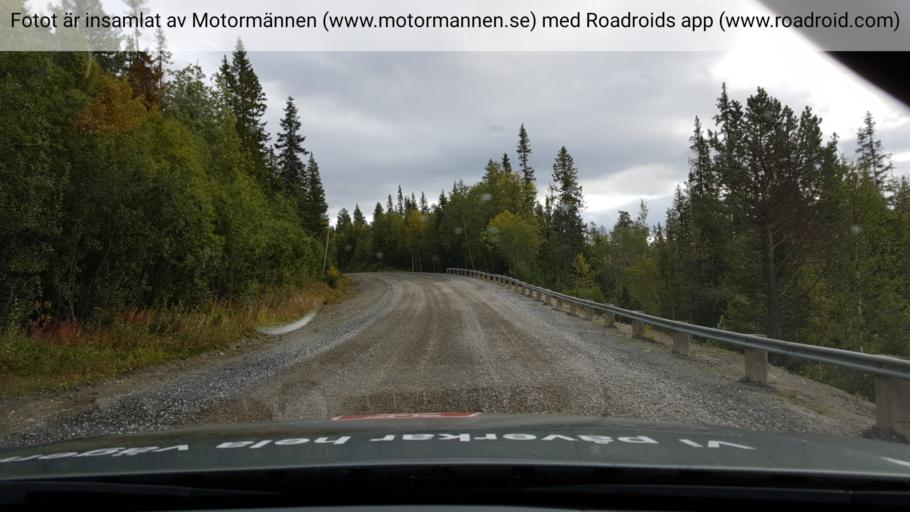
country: NO
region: Nord-Trondelag
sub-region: Snasa
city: Snaase
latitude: 63.7300
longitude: 12.5674
